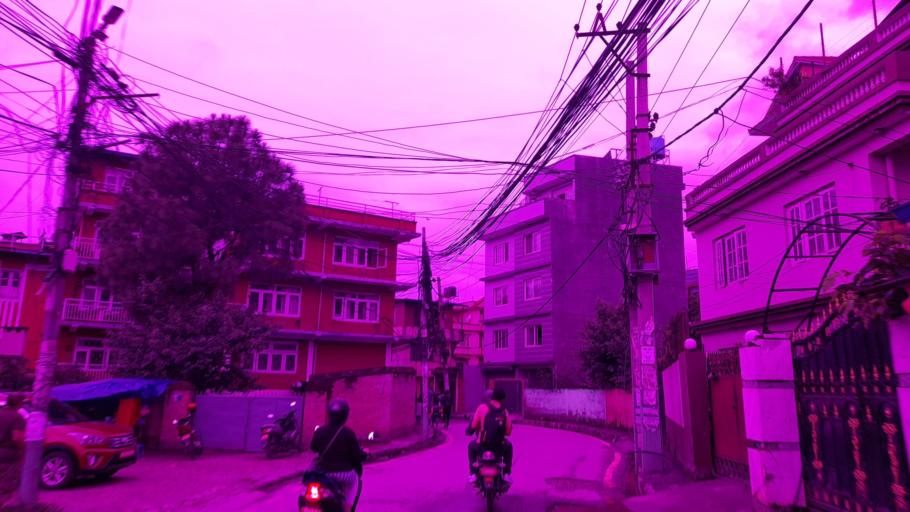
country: NP
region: Central Region
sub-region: Bagmati Zone
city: Kathmandu
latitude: 27.7012
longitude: 85.2955
